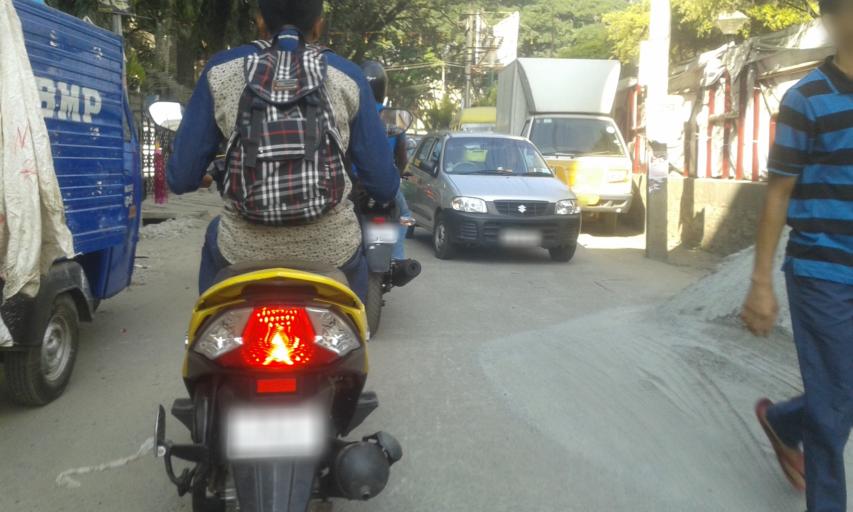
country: IN
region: Karnataka
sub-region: Bangalore Urban
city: Bangalore
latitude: 12.9311
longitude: 77.6014
